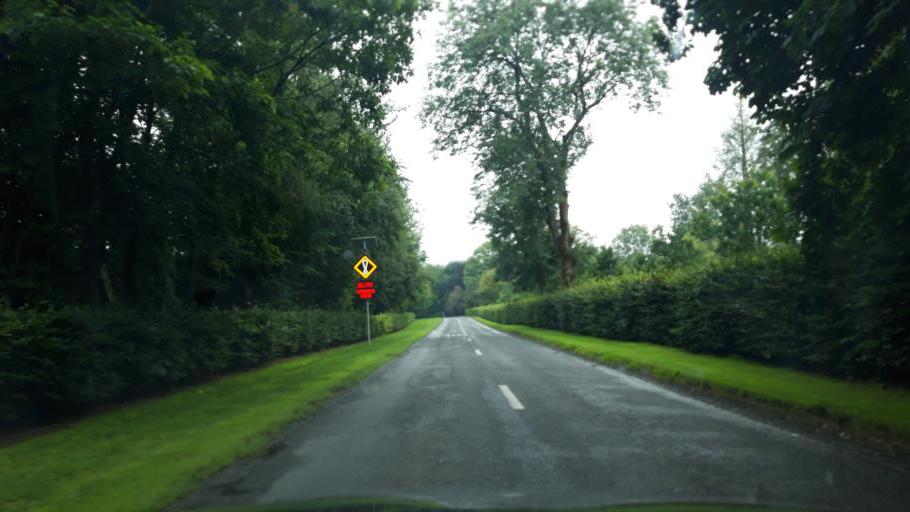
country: IE
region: Munster
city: Fethard
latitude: 52.5089
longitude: -7.6857
